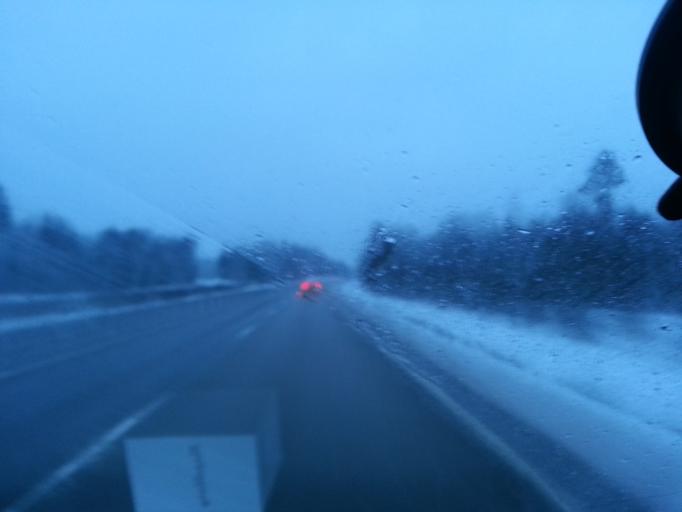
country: SE
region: Kronoberg
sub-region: Ljungby Kommun
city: Lagan
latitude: 56.9801
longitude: 14.0186
